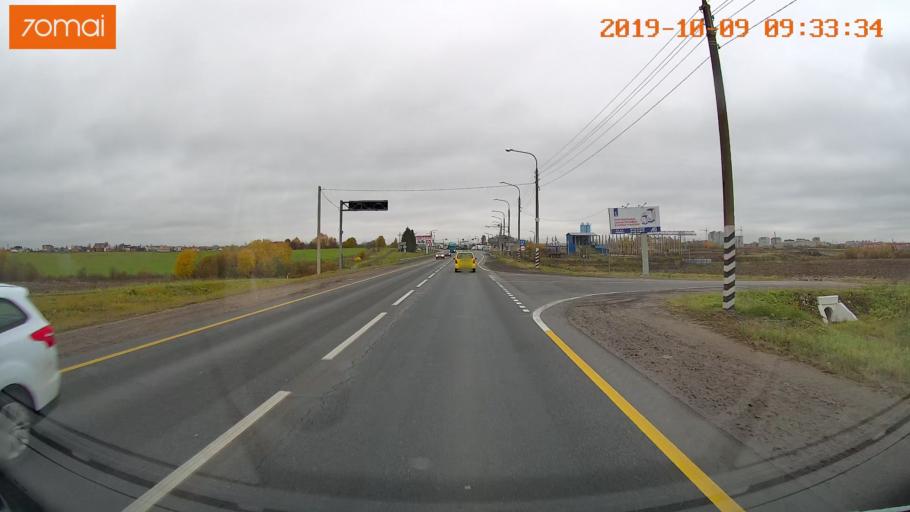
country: RU
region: Vologda
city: Vologda
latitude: 59.1692
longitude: 39.9122
